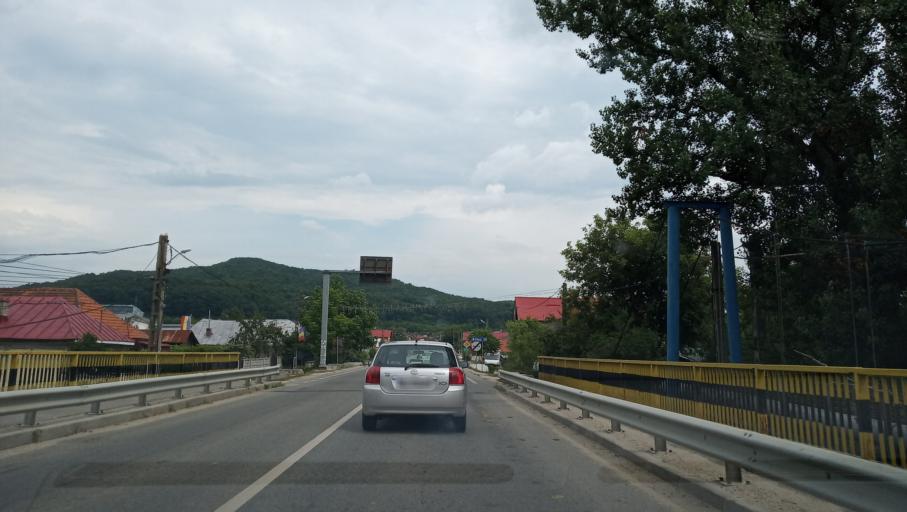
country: RO
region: Gorj
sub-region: Comuna Balteni
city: Pesteana Jiu
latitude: 44.8477
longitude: 23.2986
